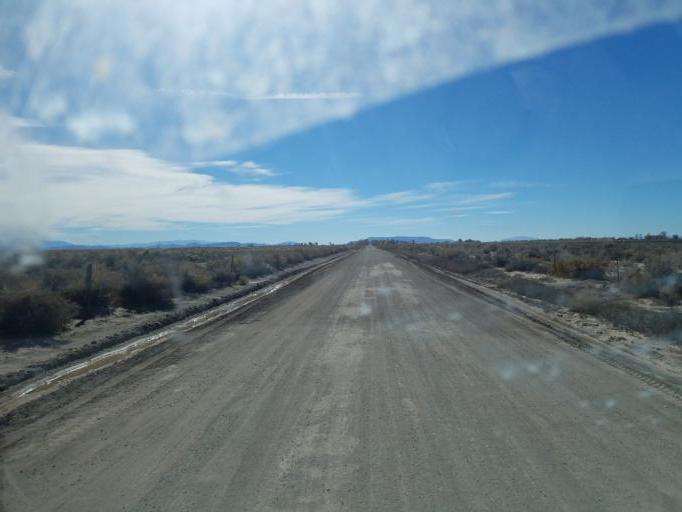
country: US
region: Colorado
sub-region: Alamosa County
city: Alamosa East
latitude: 37.5027
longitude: -105.7847
